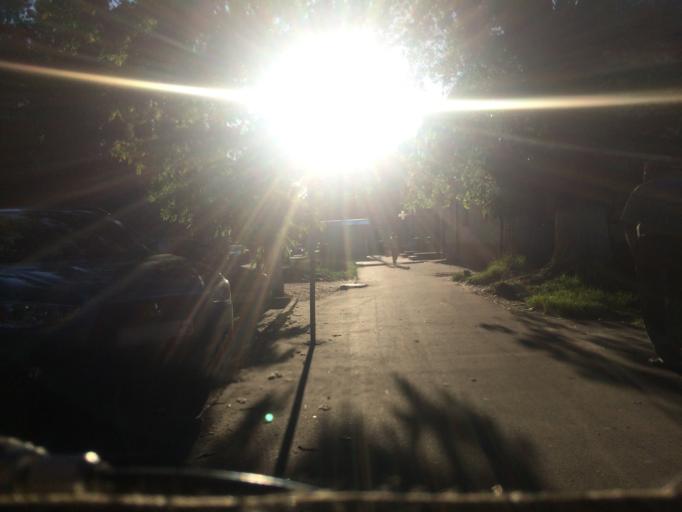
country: RU
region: Kursk
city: Kursk
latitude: 51.6718
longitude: 36.1525
